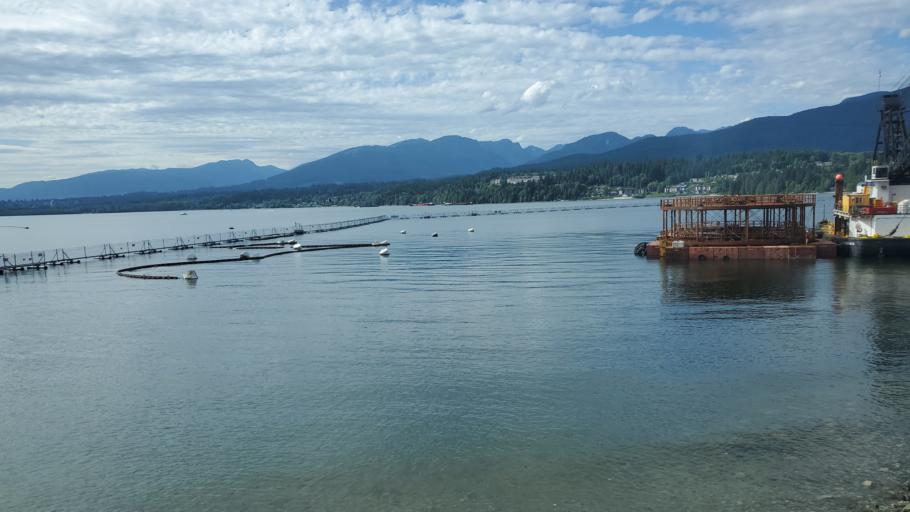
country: CA
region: British Columbia
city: Burnaby
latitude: 49.2886
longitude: -122.9566
